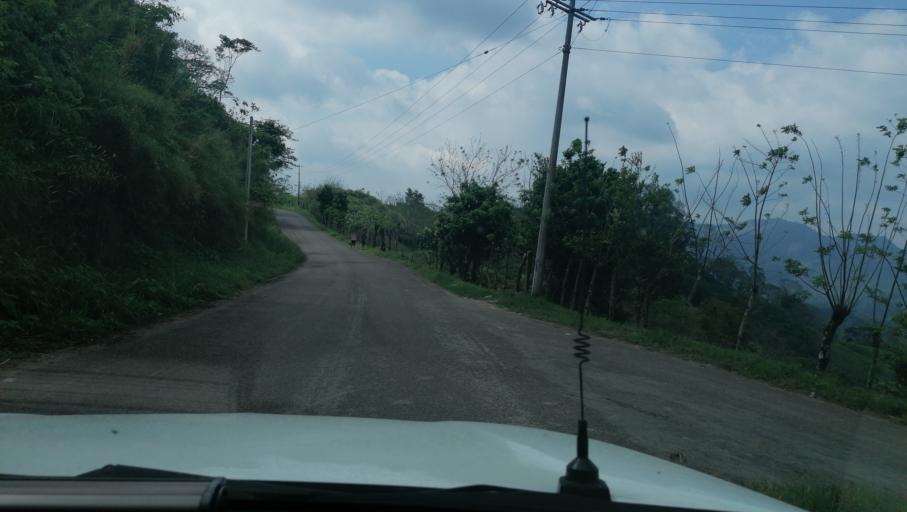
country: MX
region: Chiapas
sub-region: Francisco Leon
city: San Miguel la Sardina
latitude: 17.2387
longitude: -93.3156
